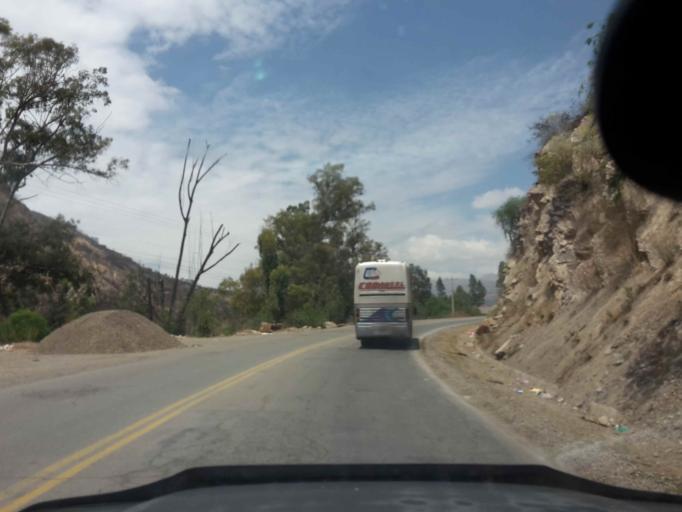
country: BO
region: Cochabamba
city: Sipe Sipe
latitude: -17.5386
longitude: -66.3354
